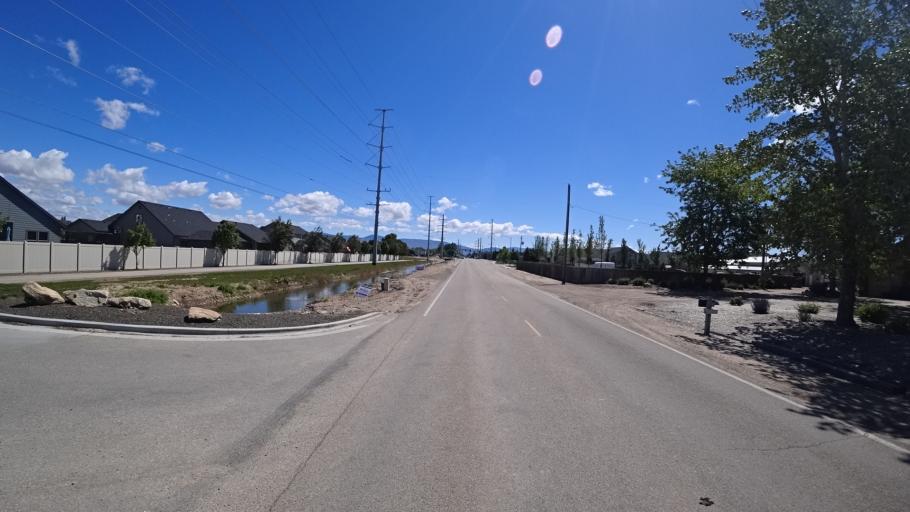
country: US
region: Idaho
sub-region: Ada County
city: Meridian
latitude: 43.6484
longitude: -116.3778
